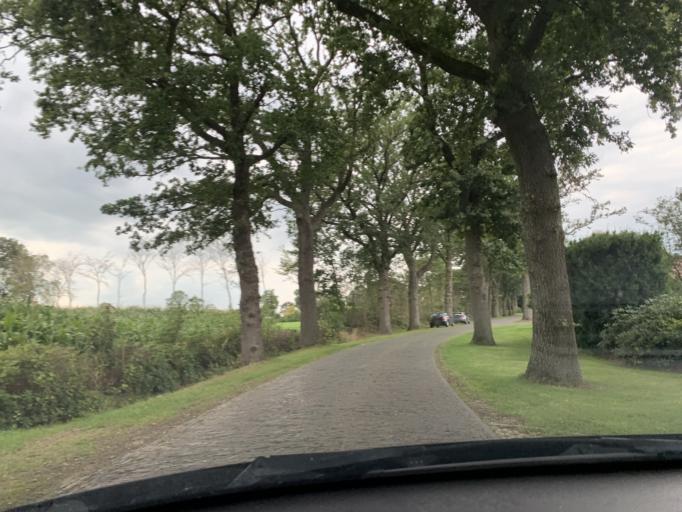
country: DE
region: Lower Saxony
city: Westerstede
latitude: 53.2432
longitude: 7.8937
